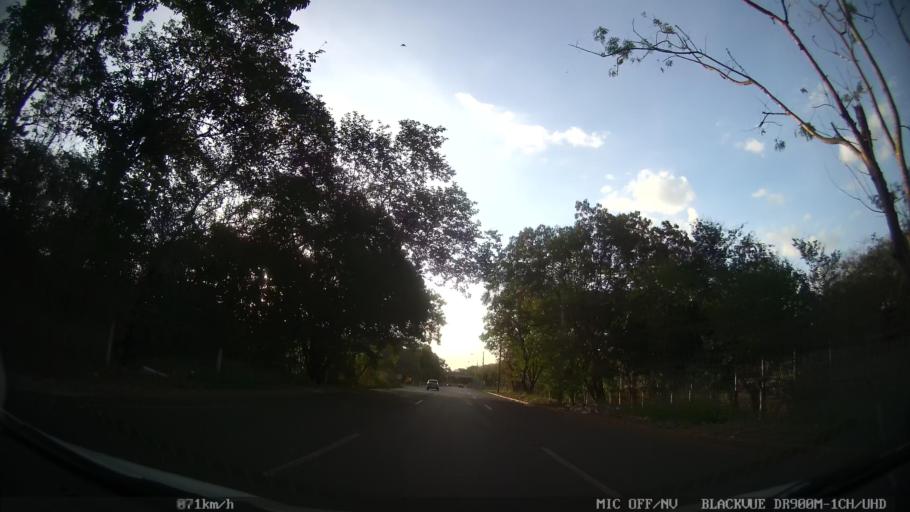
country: BR
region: Sao Paulo
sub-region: Ribeirao Preto
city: Ribeirao Preto
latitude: -21.1098
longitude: -47.8085
